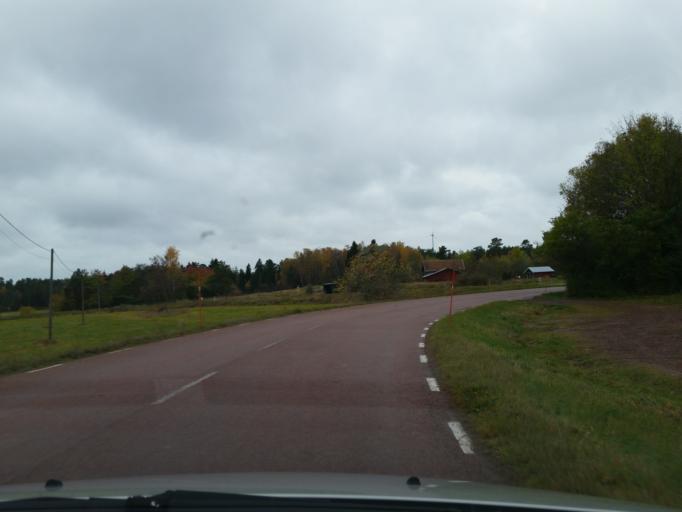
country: AX
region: Alands landsbygd
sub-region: Lumparland
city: Lumparland
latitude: 60.1158
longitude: 20.2638
